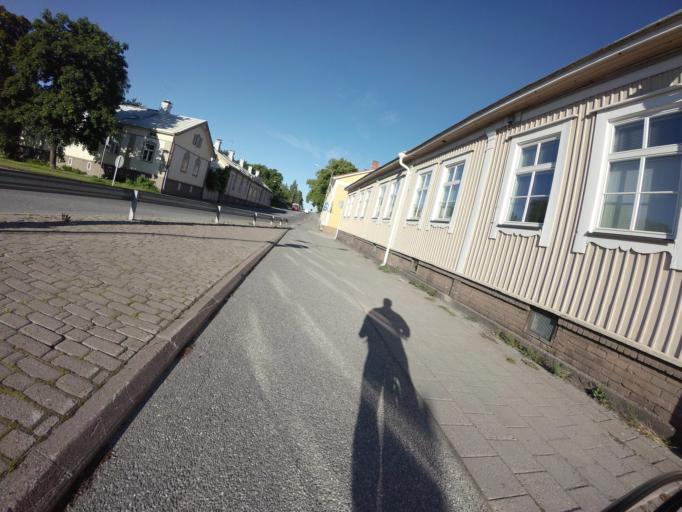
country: FI
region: Varsinais-Suomi
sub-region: Turku
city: Turku
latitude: 60.4600
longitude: 22.2620
